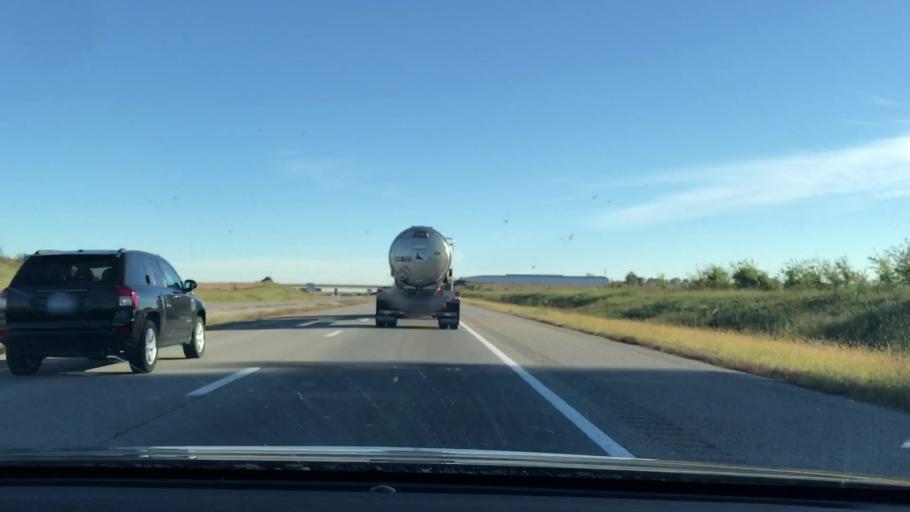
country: US
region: Kentucky
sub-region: Christian County
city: Hopkinsville
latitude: 36.7584
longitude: -87.5046
